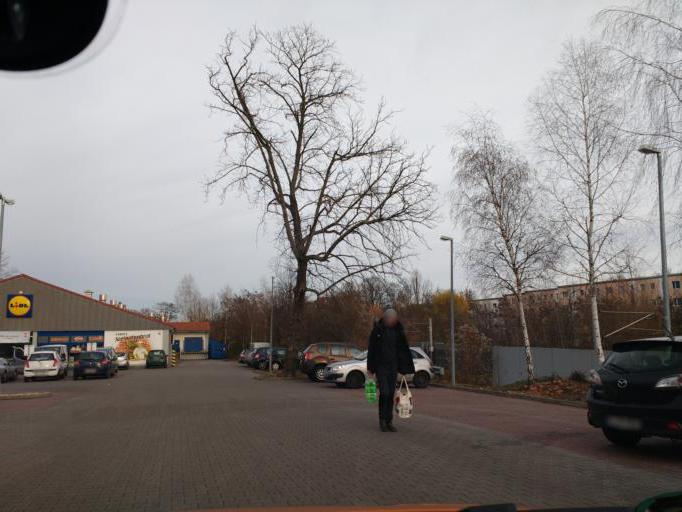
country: DE
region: Berlin
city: Lankwitz
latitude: 52.4494
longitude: 13.3543
